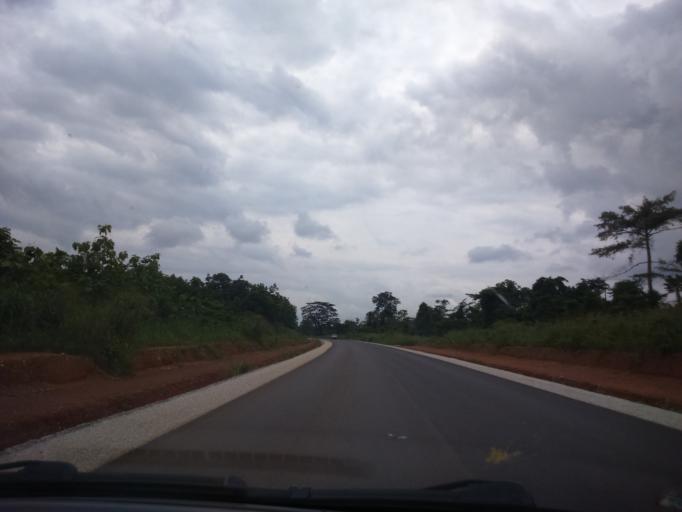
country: CI
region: Lagunes
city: Akoupe
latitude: 6.3216
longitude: -3.8336
